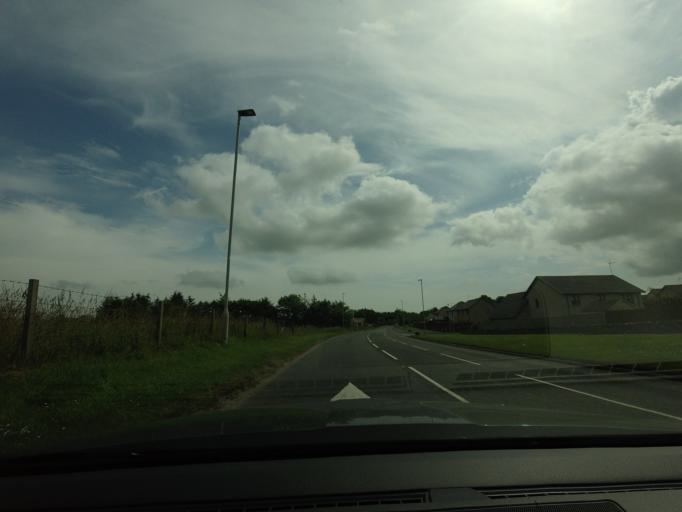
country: GB
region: Scotland
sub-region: Aberdeenshire
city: Mintlaw
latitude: 57.5200
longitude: -1.9489
